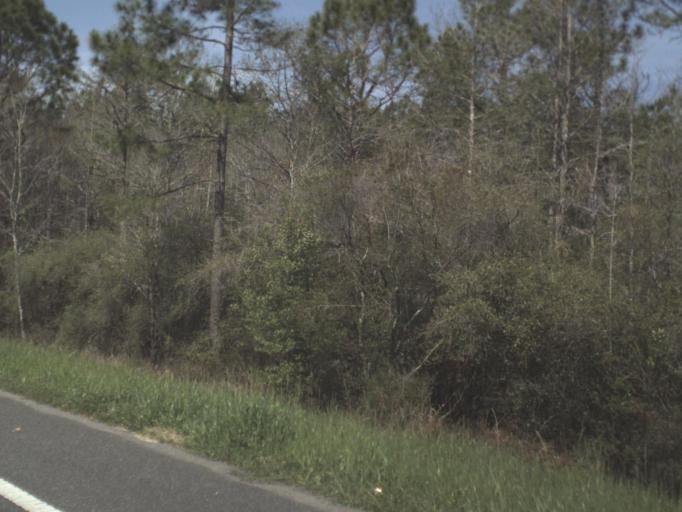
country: US
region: Florida
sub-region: Holmes County
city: Bonifay
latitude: 30.7949
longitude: -85.7258
